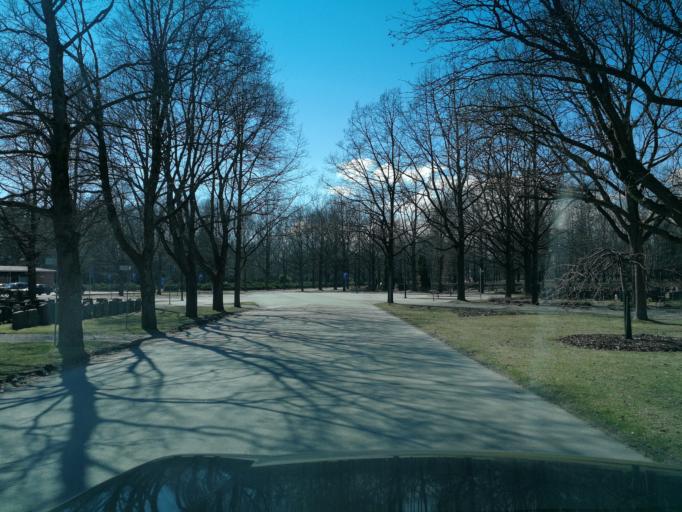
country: FI
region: Uusimaa
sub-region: Helsinki
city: Vantaa
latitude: 60.2349
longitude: 25.0263
